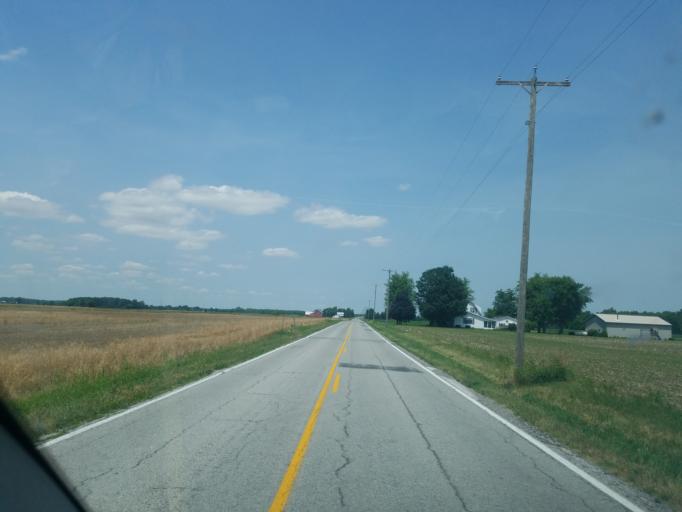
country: US
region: Ohio
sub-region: Wyandot County
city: Carey
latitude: 40.9565
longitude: -83.4861
